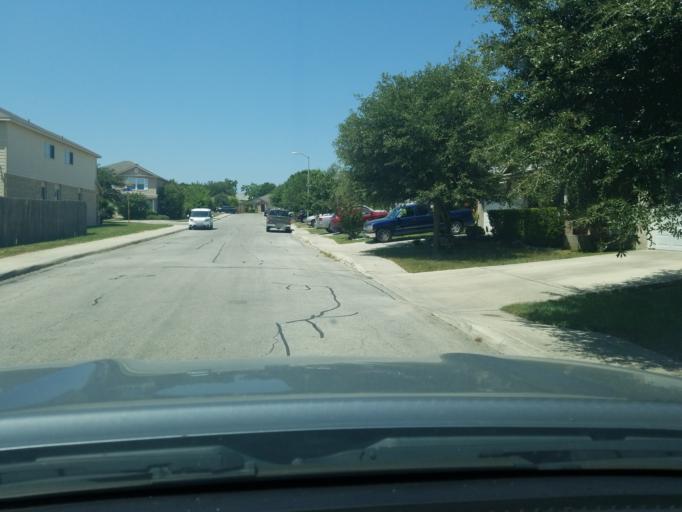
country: US
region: Texas
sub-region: Bexar County
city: Timberwood Park
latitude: 29.7009
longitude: -98.4830
